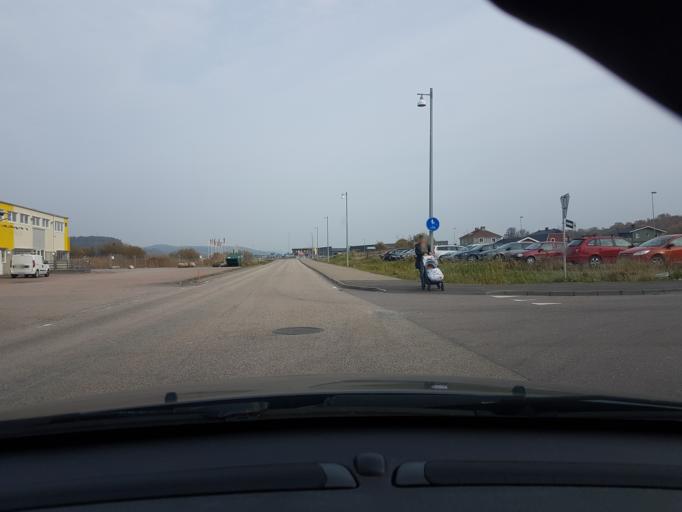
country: SE
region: Vaestra Goetaland
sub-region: Ale Kommun
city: Alvangen
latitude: 57.9618
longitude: 12.1279
